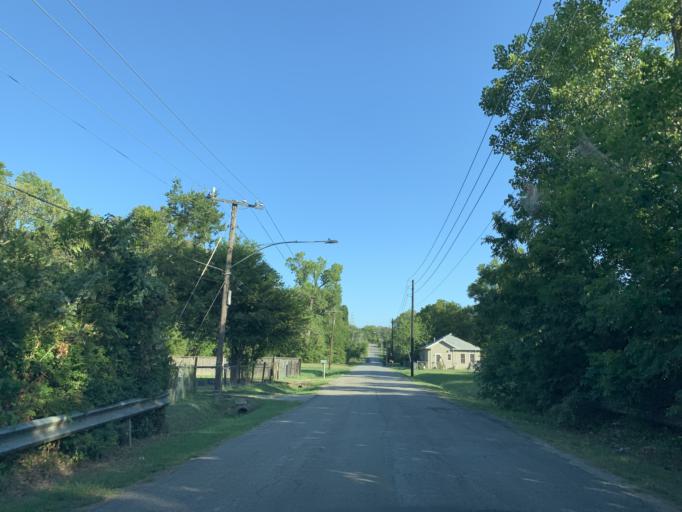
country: US
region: Texas
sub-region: Dallas County
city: Hutchins
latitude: 32.6717
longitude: -96.7748
